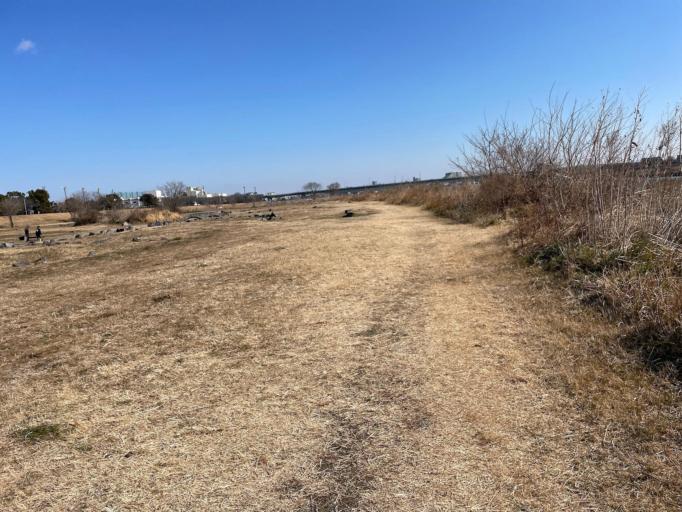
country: JP
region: Tokyo
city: Chofugaoka
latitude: 35.6525
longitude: 139.5037
